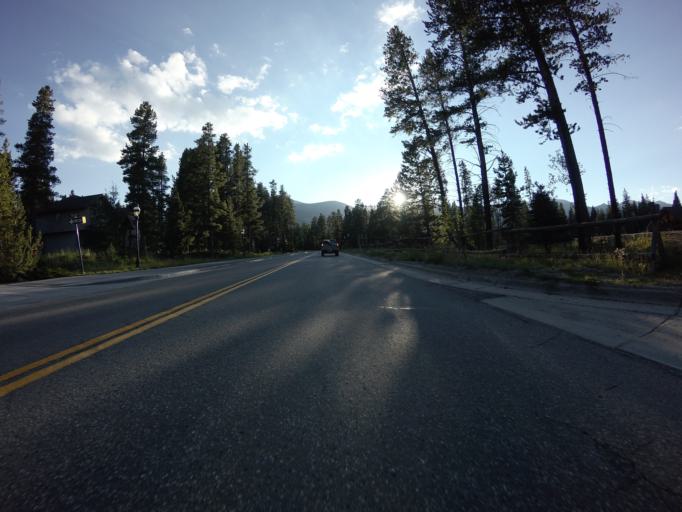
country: US
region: Colorado
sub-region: Summit County
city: Breckenridge
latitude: 39.4837
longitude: -106.0568
